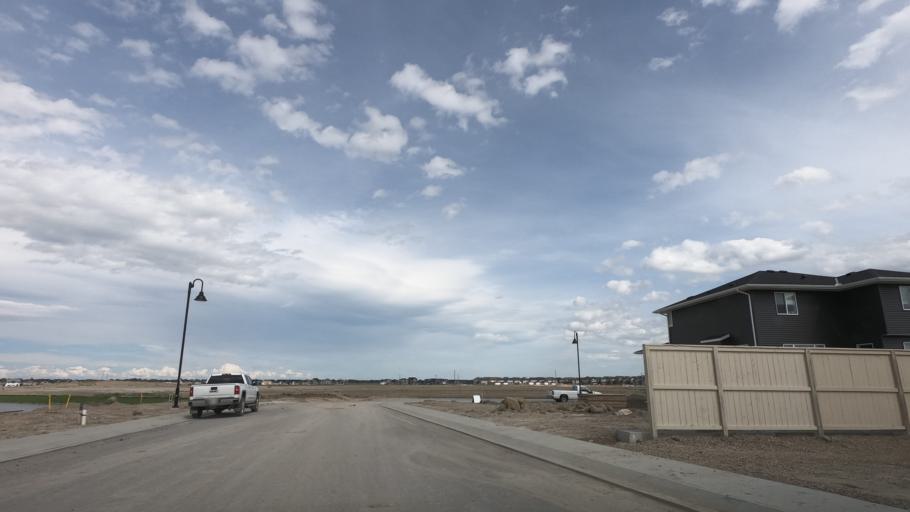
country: CA
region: Alberta
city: Airdrie
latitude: 51.2807
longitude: -114.0415
